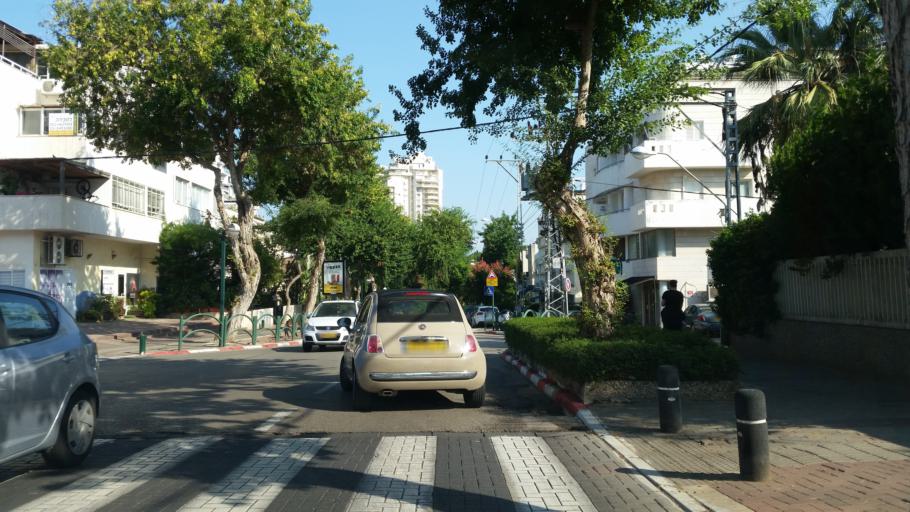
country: IL
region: Tel Aviv
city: Ramat HaSharon
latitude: 32.1470
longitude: 34.8454
